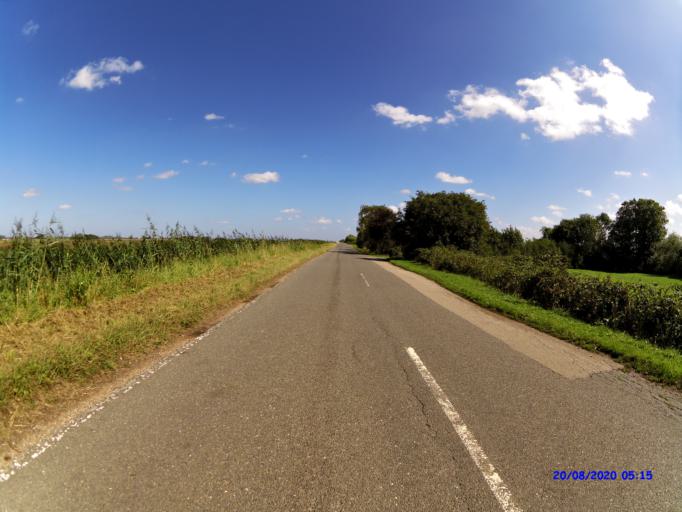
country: GB
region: England
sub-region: Cambridgeshire
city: Whittlesey
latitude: 52.5225
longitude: -0.1166
